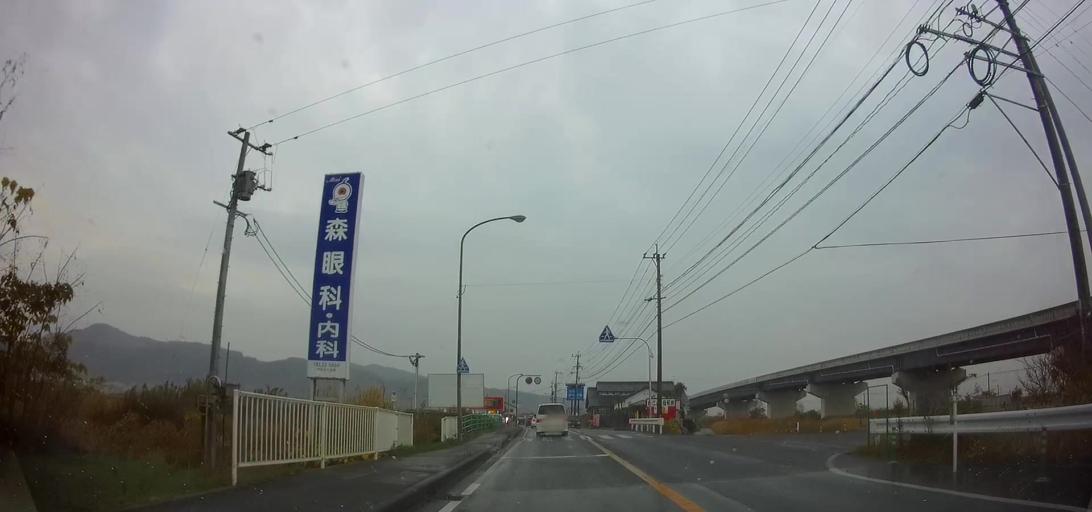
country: JP
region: Nagasaki
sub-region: Isahaya-shi
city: Isahaya
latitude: 32.8343
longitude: 130.1257
